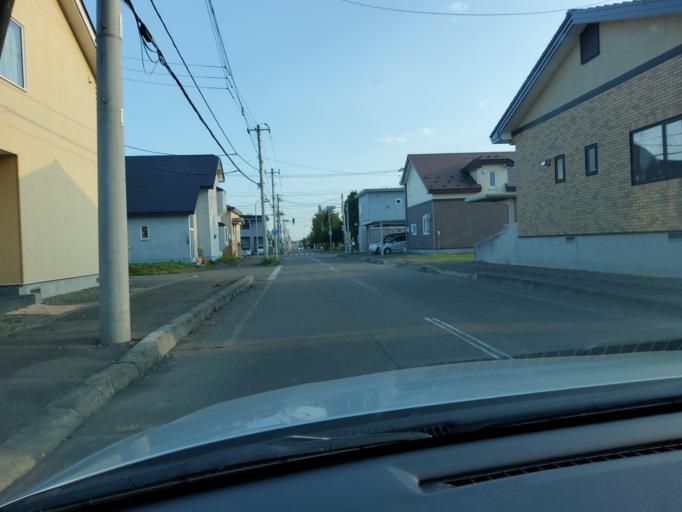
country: JP
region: Hokkaido
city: Obihiro
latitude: 42.9412
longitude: 143.1823
